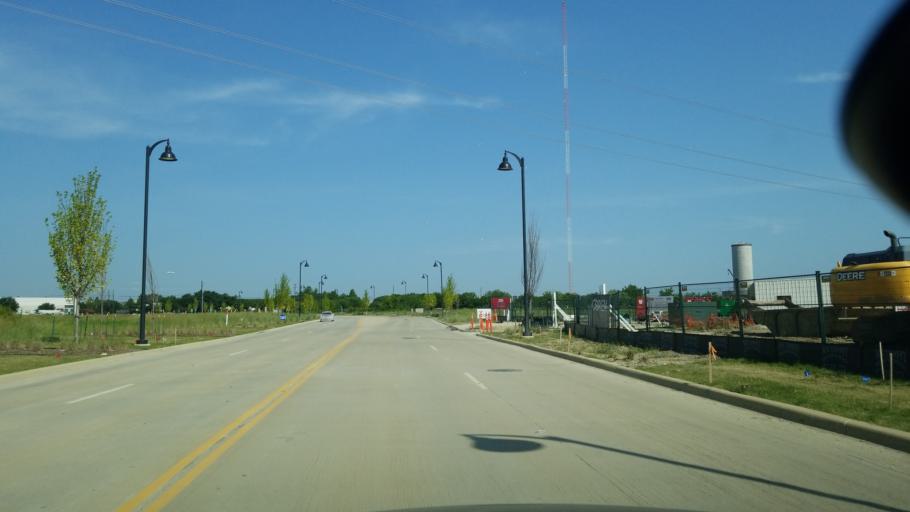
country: US
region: Texas
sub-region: Dallas County
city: Coppell
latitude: 32.9389
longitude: -96.9893
